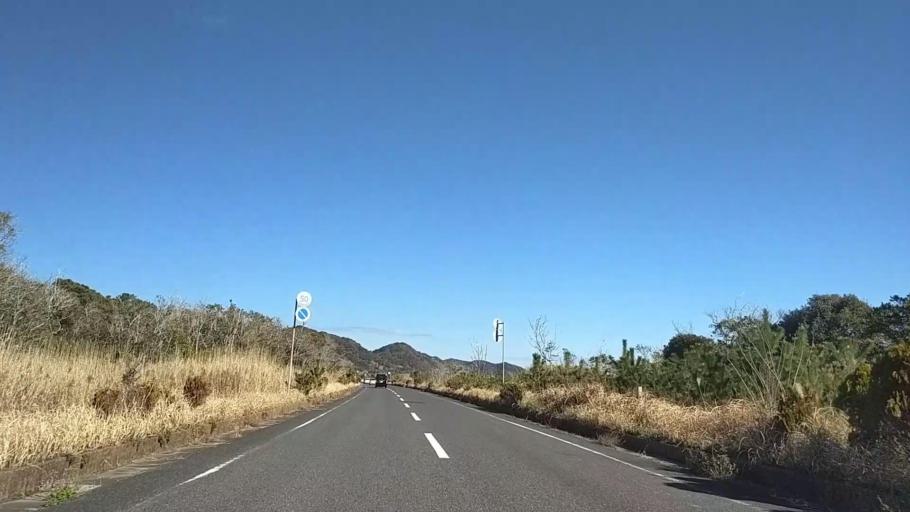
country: JP
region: Chiba
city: Tateyama
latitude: 35.0192
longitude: 139.9875
